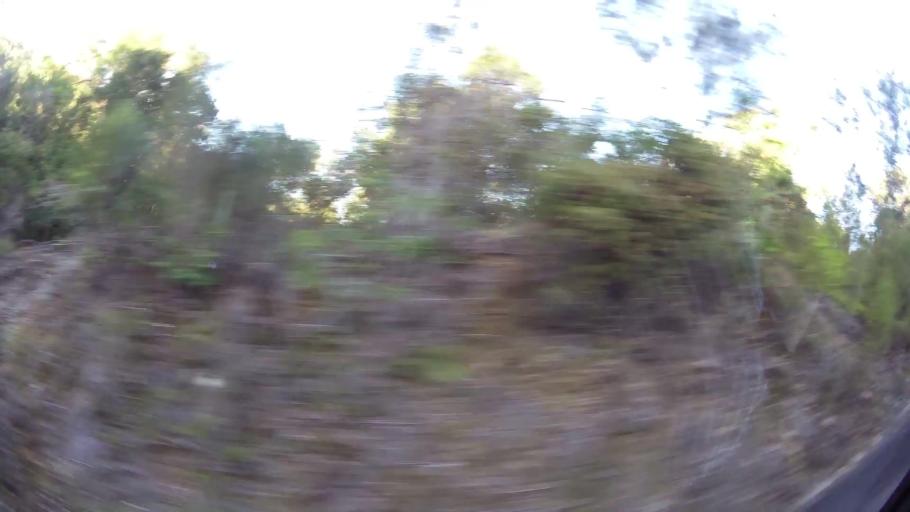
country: ZA
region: Western Cape
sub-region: Eden District Municipality
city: George
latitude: -33.9892
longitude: 22.5838
